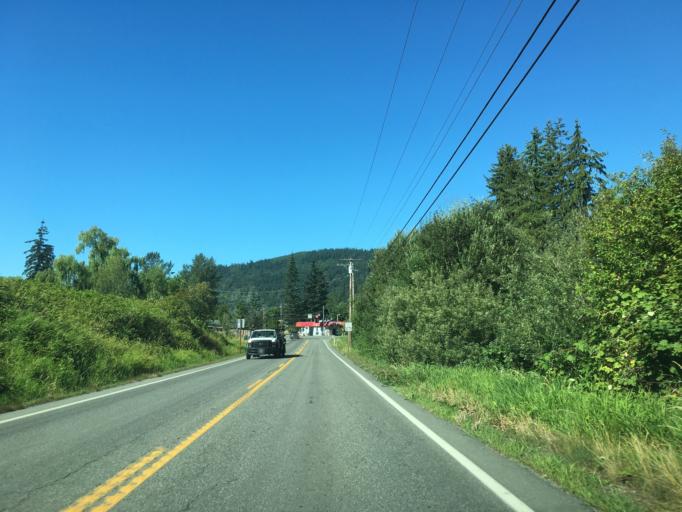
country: US
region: Washington
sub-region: Skagit County
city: Clear Lake
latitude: 48.4552
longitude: -122.2359
